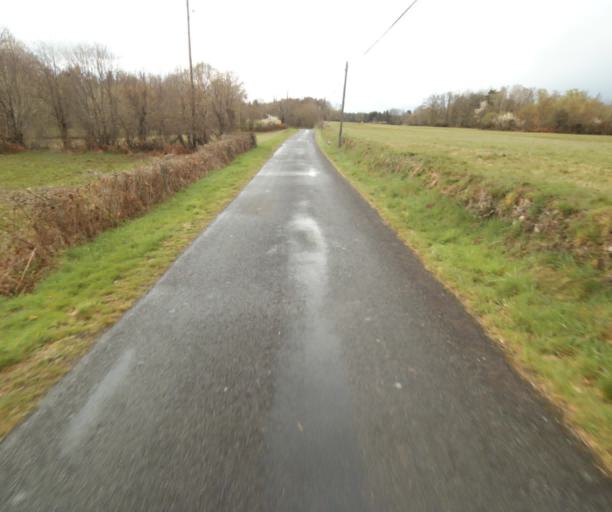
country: FR
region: Limousin
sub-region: Departement de la Correze
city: Saint-Privat
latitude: 45.2217
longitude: 2.0166
